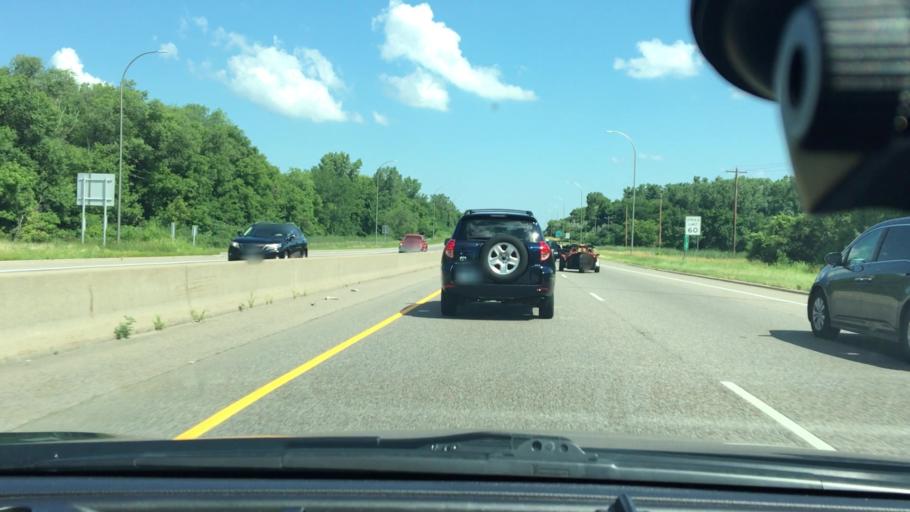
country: US
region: Minnesota
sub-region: Hennepin County
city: New Hope
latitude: 45.0702
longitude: -93.4011
